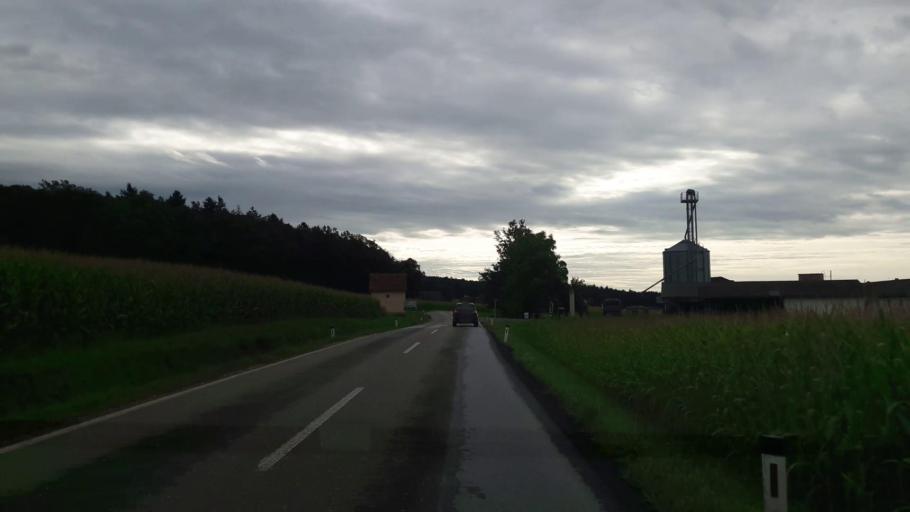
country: AT
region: Styria
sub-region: Politischer Bezirk Hartberg-Fuerstenfeld
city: Kaindorf
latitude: 47.2147
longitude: 15.9256
